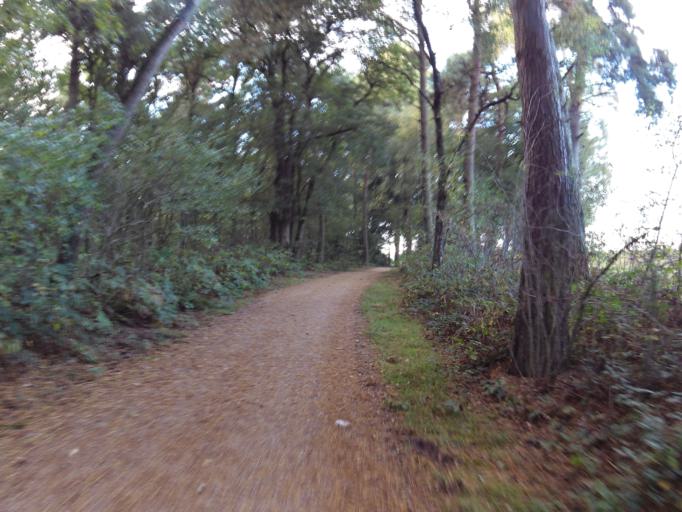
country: NL
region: Limburg
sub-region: Gemeente Bergen
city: Wellerlooi
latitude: 51.5619
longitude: 6.1189
